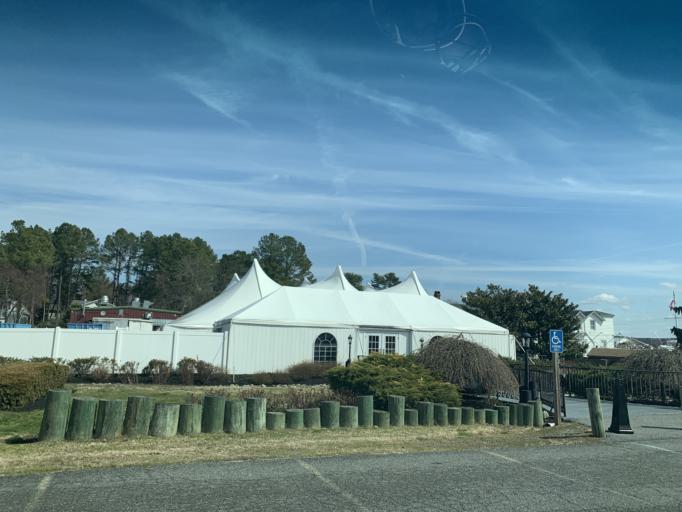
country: US
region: Maryland
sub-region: Cecil County
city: Charlestown
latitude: 39.5726
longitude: -75.9732
